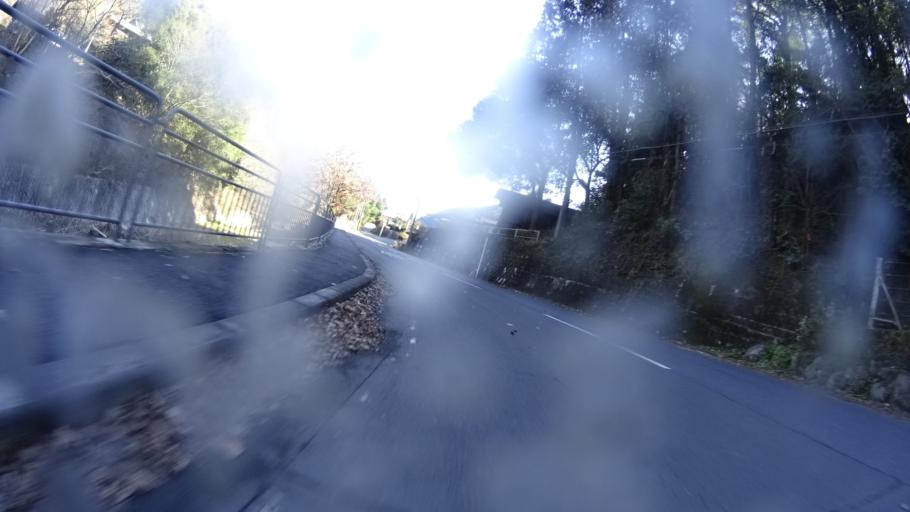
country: JP
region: Yamanashi
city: Uenohara
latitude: 35.6239
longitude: 139.1509
